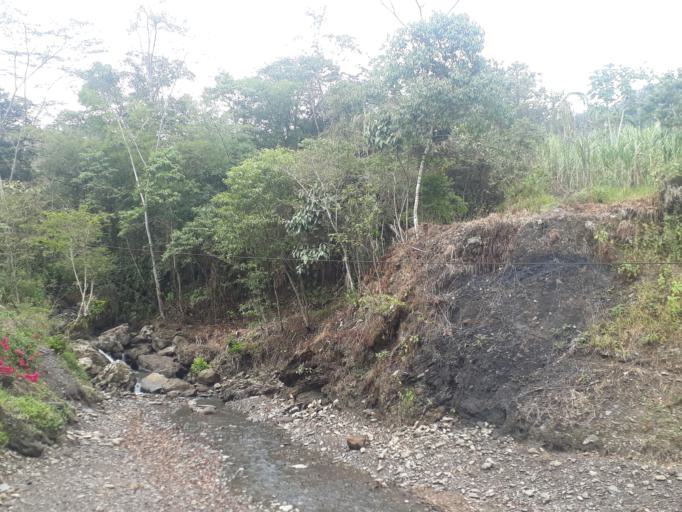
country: CO
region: Boyaca
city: Maripi
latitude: 5.5434
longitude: -74.0096
